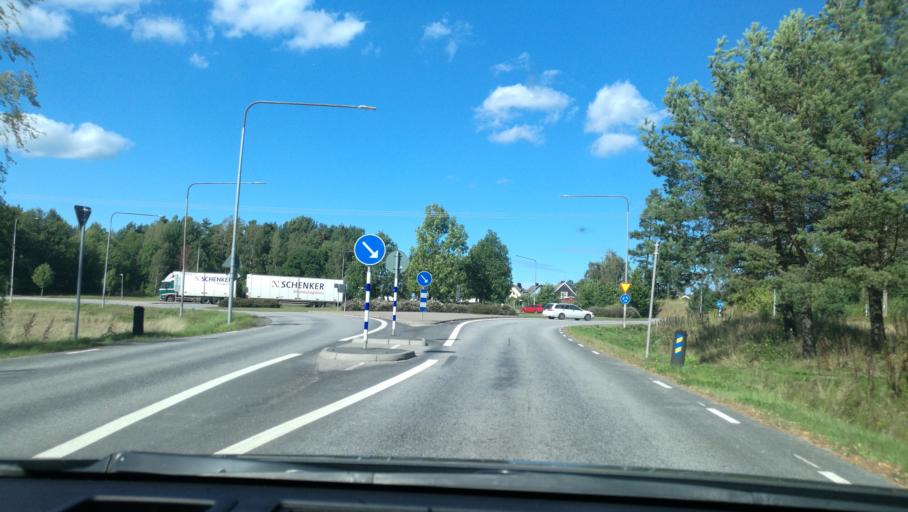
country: SE
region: Vaestra Goetaland
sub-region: Mariestads Kommun
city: Mariestad
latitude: 58.6916
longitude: 13.8420
